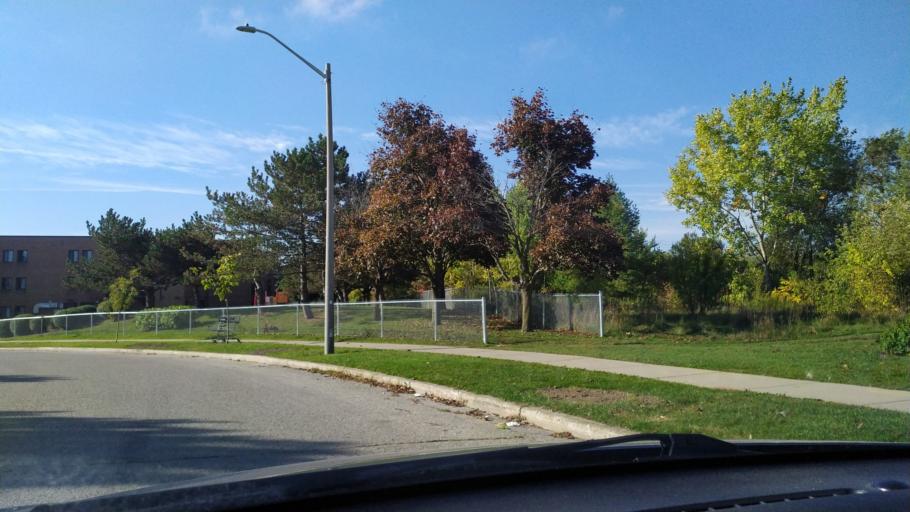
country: CA
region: Ontario
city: Waterloo
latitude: 43.4949
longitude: -80.5248
